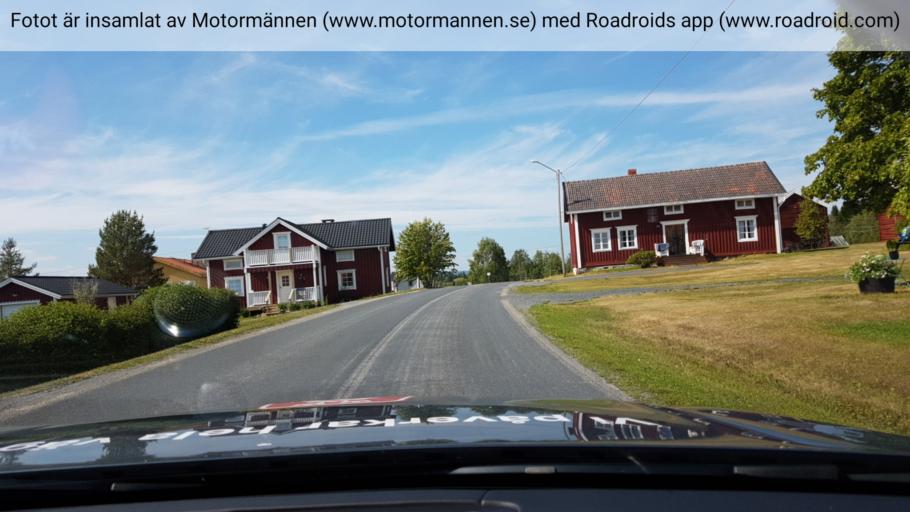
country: SE
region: Jaemtland
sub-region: Krokoms Kommun
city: Valla
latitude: 63.3032
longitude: 13.8720
